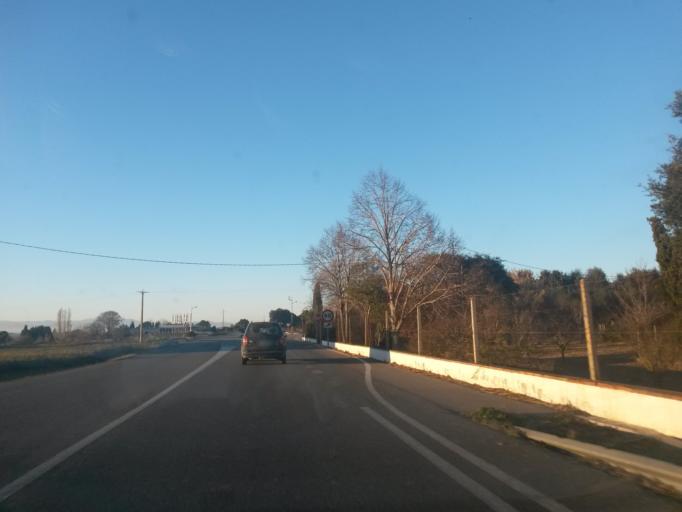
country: ES
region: Catalonia
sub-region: Provincia de Girona
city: Regencos
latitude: 41.9541
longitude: 3.1584
